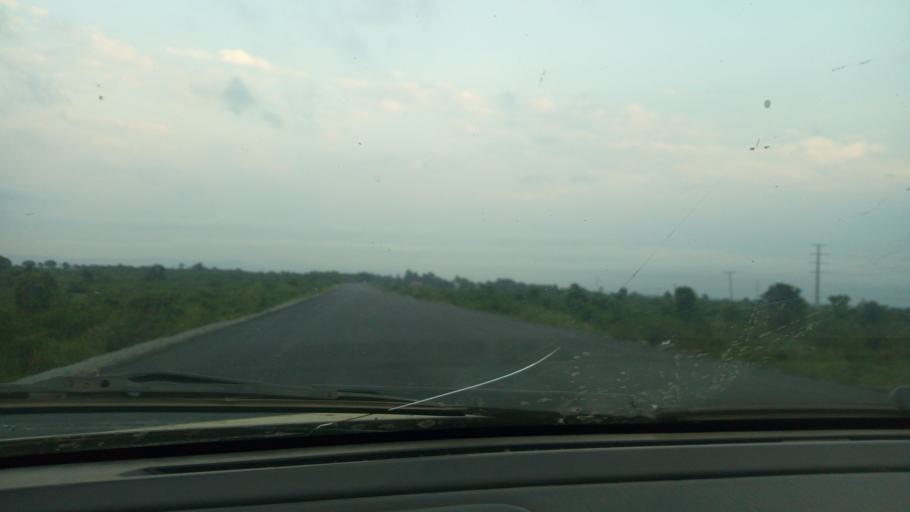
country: UG
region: Western Region
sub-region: Rubirizi District
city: Rubirizi
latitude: -0.1412
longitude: 30.0600
